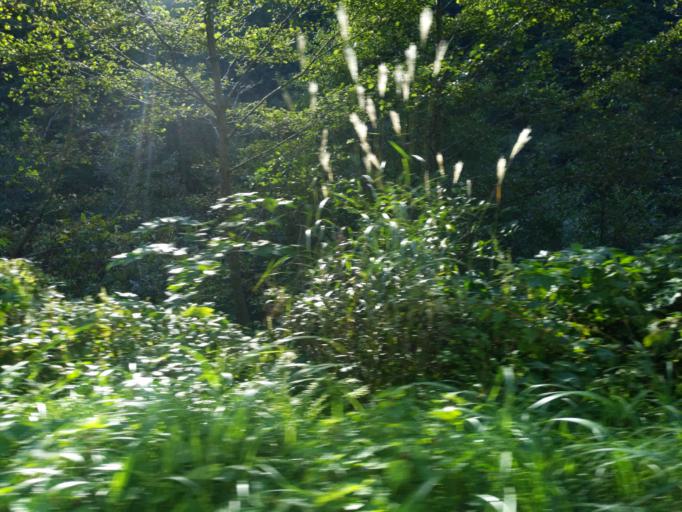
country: JP
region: Toyama
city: Kamiichi
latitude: 36.5167
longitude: 137.4495
